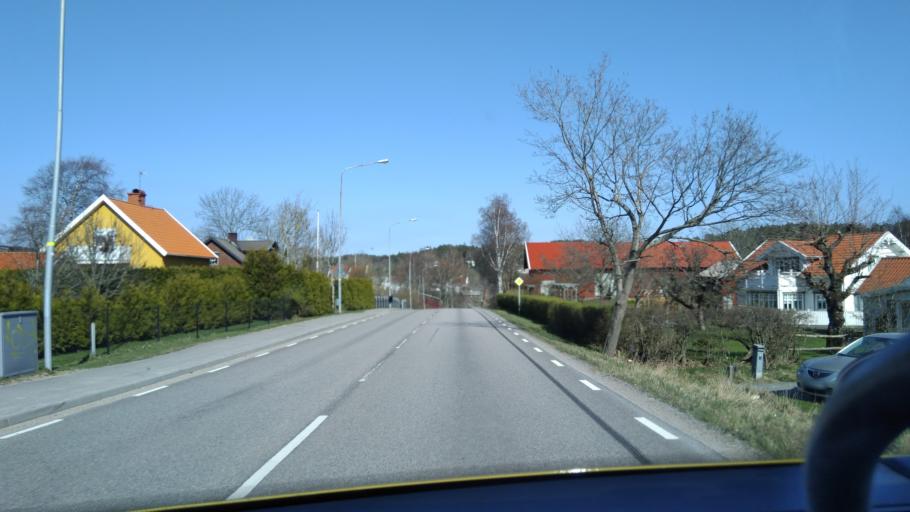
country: SE
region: Vaestra Goetaland
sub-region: Orust
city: Henan
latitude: 58.2336
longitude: 11.6732
